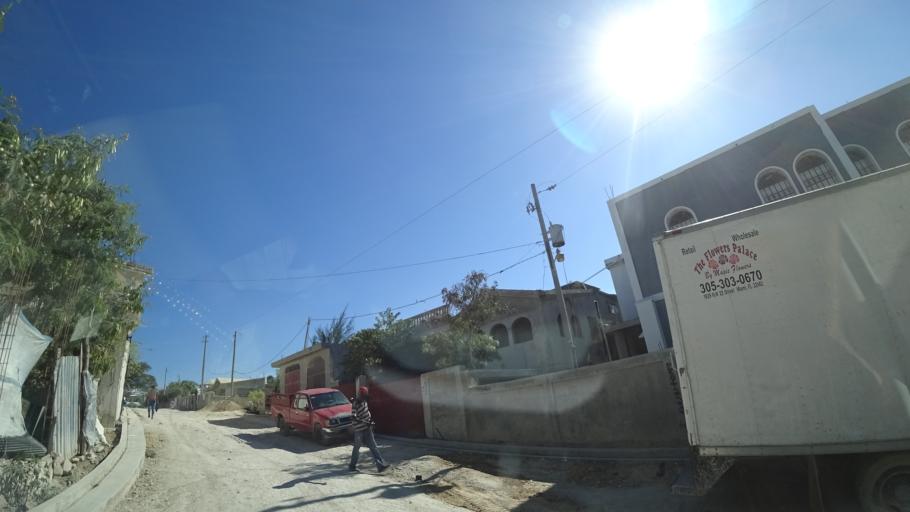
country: HT
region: Ouest
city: Delmas 73
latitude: 18.5565
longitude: -72.2856
